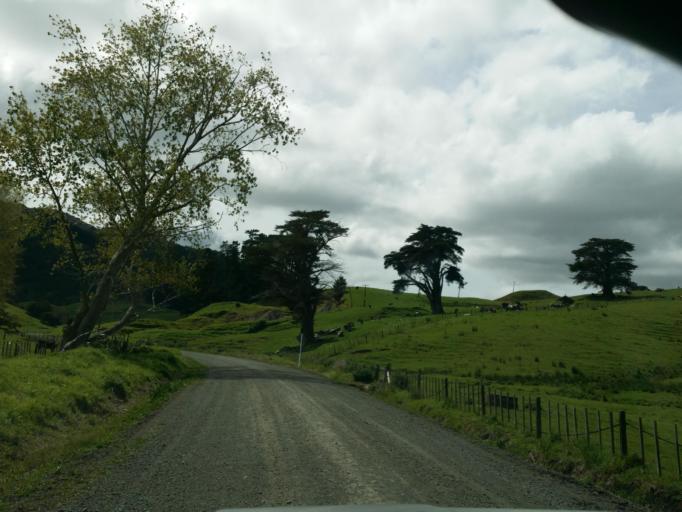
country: NZ
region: Northland
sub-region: Kaipara District
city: Dargaville
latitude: -35.8790
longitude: 174.0455
